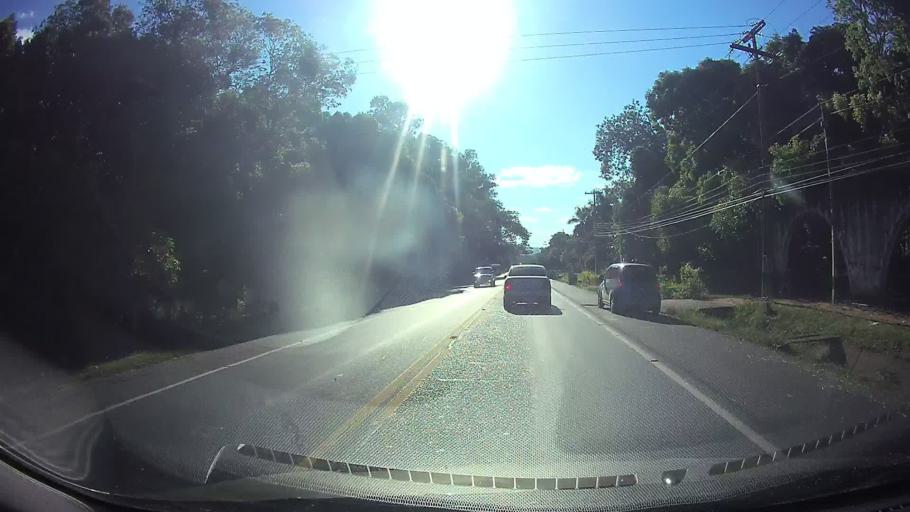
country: PY
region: Cordillera
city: Caacupe
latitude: -25.3724
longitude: -57.2141
